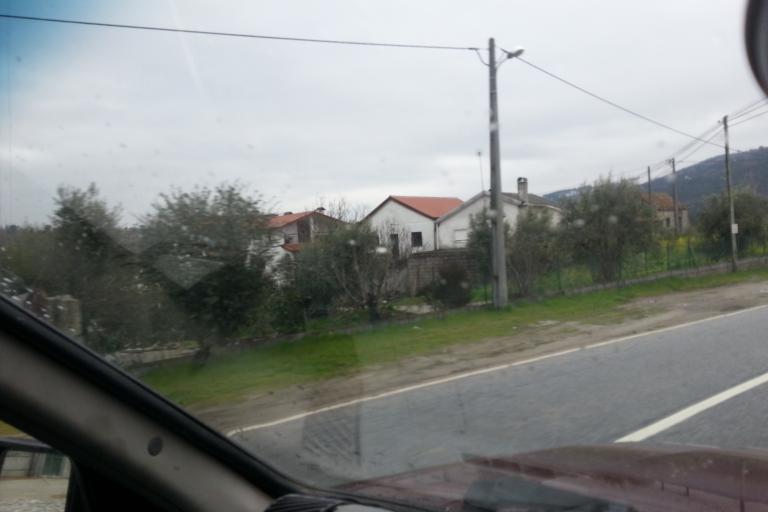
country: PT
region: Viseu
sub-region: Viseu
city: Rio de Loba
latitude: 40.6377
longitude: -7.8329
